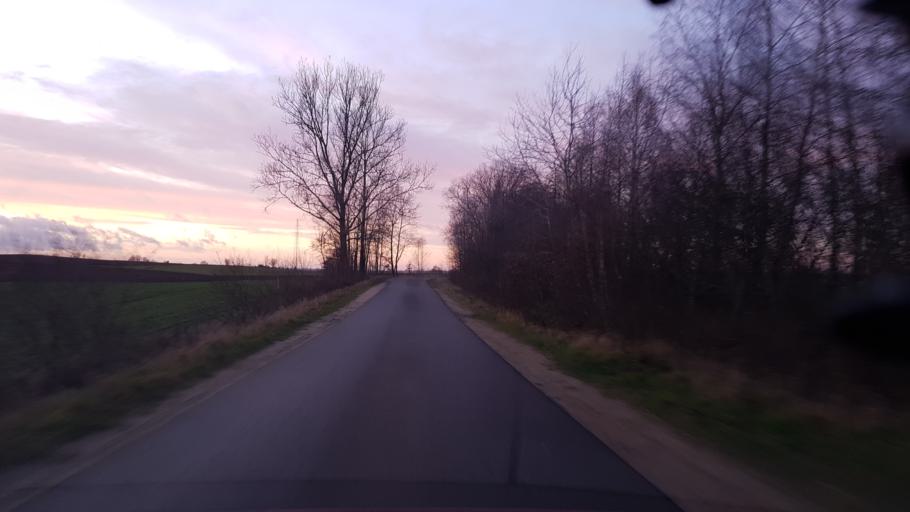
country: PL
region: Pomeranian Voivodeship
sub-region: Powiat bytowski
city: Tuchomie
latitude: 54.1279
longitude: 17.3737
